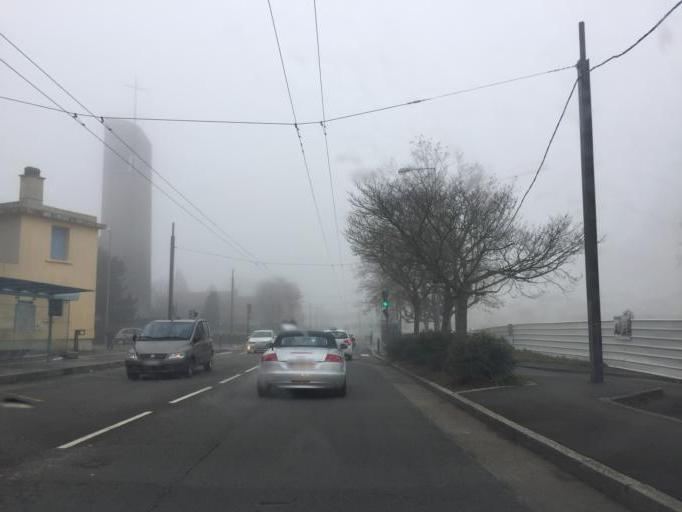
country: FR
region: Rhone-Alpes
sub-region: Departement du Rhone
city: Caluire-et-Cuire
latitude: 45.7919
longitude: 4.8437
